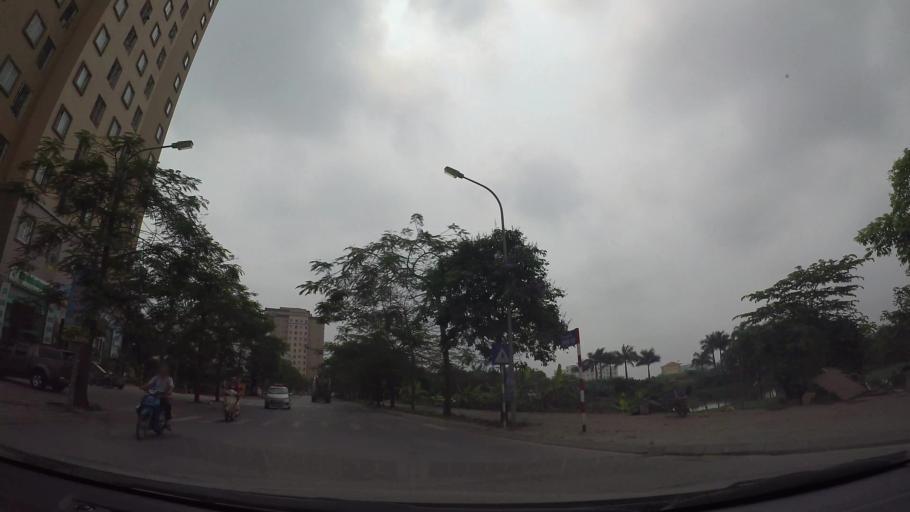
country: VN
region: Ha Noi
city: Trau Quy
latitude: 21.0587
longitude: 105.9144
